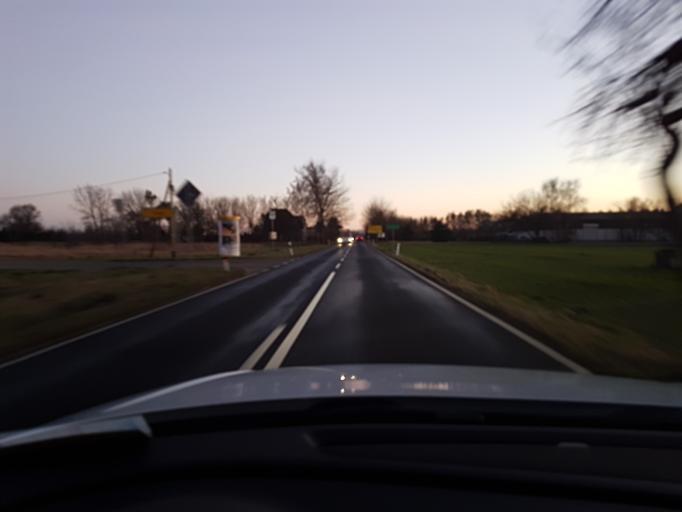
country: DE
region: Mecklenburg-Vorpommern
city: Gingst
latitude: 54.4696
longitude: 13.2964
